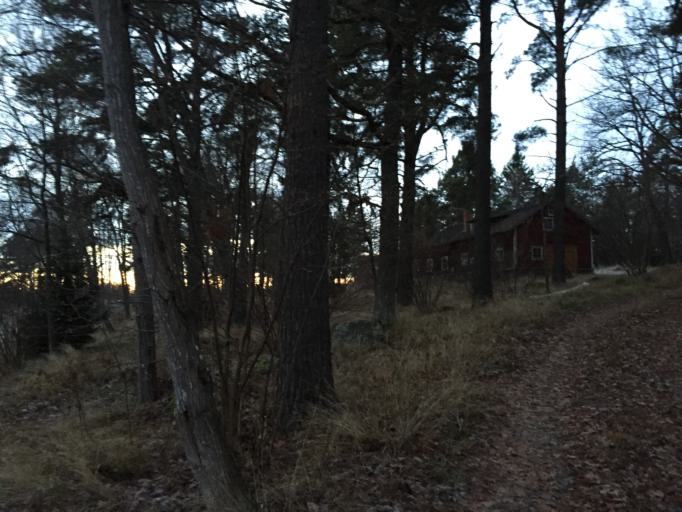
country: SE
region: Stockholm
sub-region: Salems Kommun
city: Ronninge
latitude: 59.1852
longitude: 17.7280
